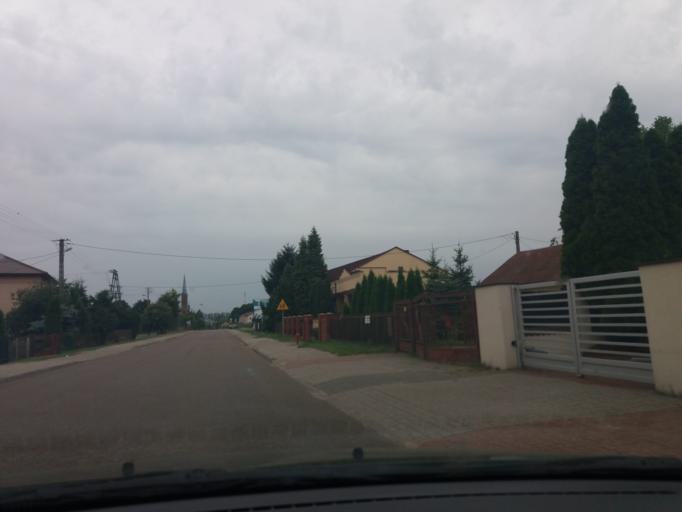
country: PL
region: Masovian Voivodeship
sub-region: Powiat mlawski
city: Wieczfnia Koscielna
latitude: 53.1971
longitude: 20.4815
